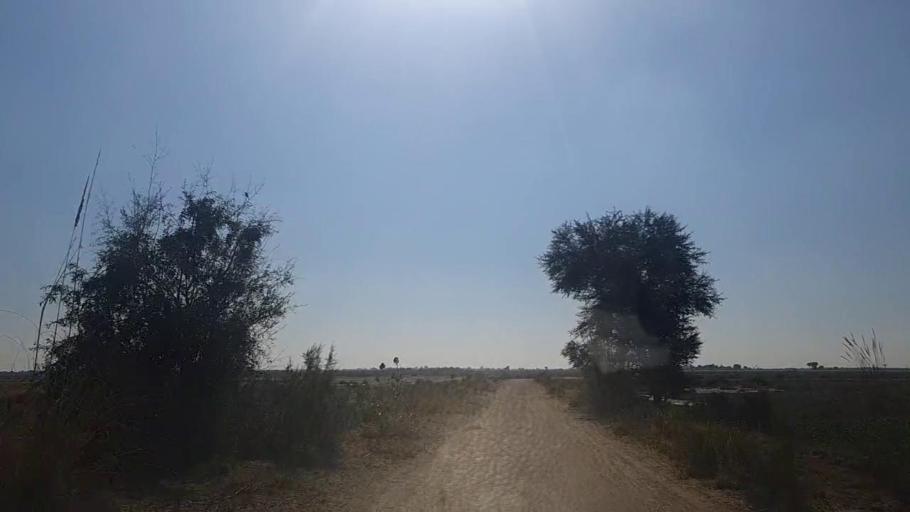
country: PK
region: Sindh
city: Sinjhoro
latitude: 26.1551
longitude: 68.8601
